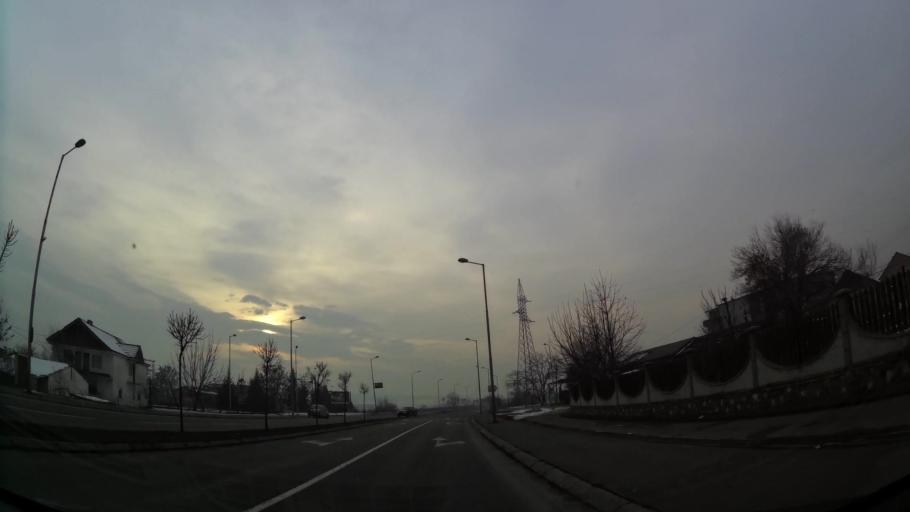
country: MK
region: Suto Orizari
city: Suto Orizare
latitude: 42.0255
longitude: 21.4127
